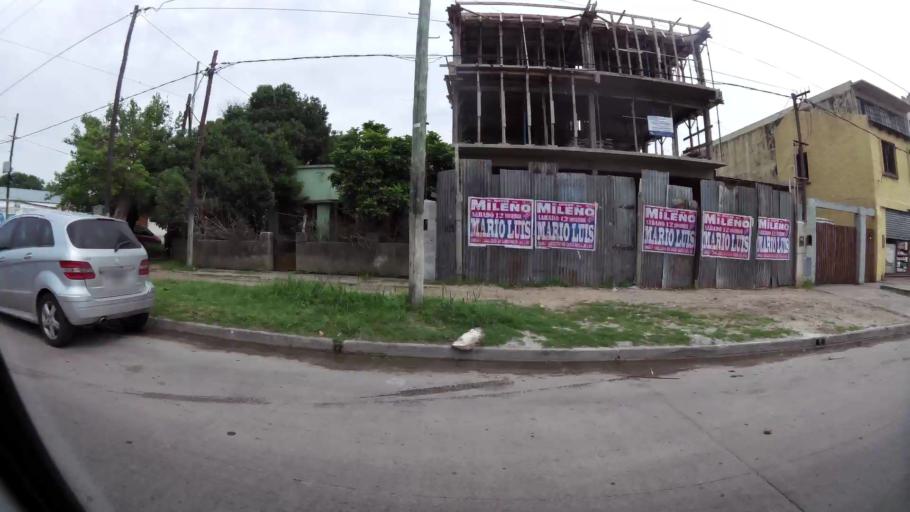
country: AR
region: Buenos Aires
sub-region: Partido de La Plata
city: La Plata
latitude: -34.9197
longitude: -58.0149
